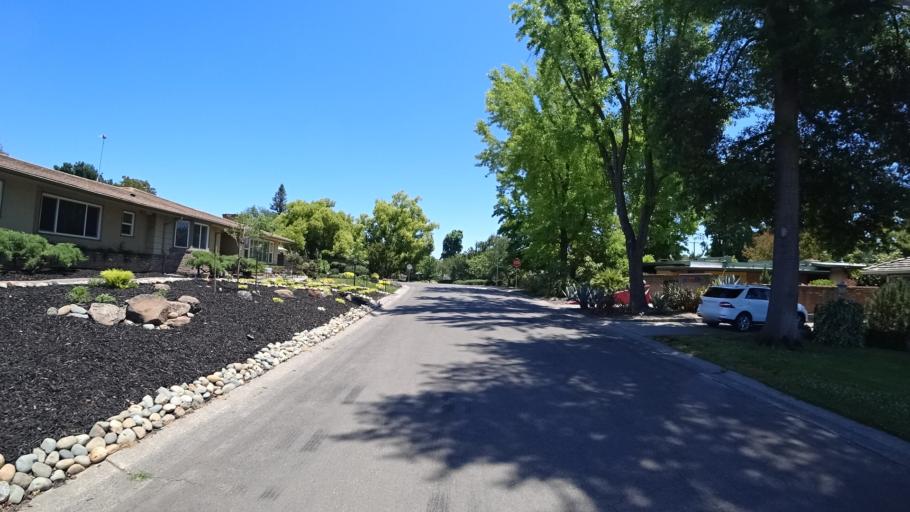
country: US
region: California
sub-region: Sacramento County
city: Sacramento
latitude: 38.5292
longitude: -121.5095
